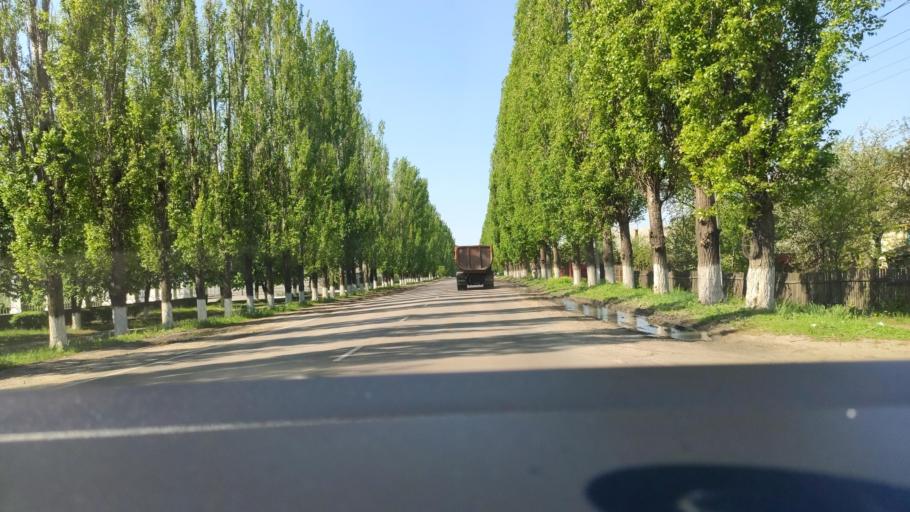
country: RU
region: Voronezj
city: Maslovka
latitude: 51.5376
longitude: 39.3341
